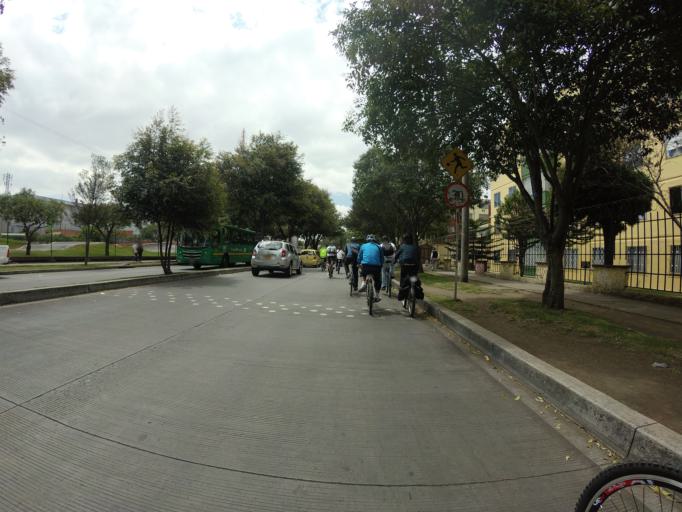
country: CO
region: Cundinamarca
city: Cota
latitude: 4.7127
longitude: -74.1126
